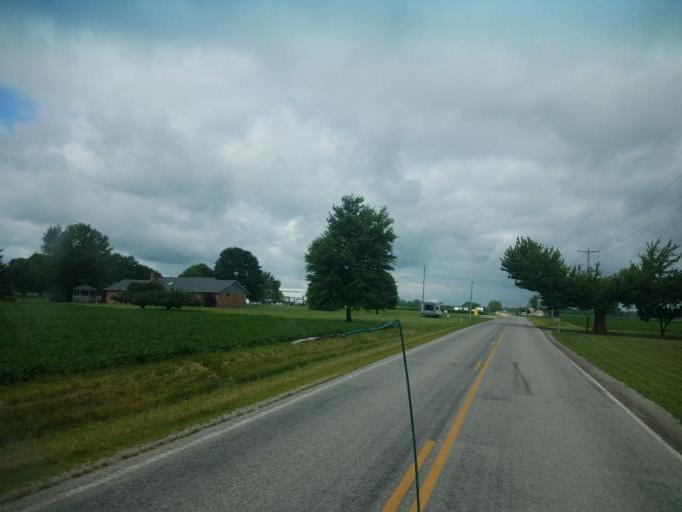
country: US
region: Ohio
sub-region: Union County
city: Richwood
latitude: 40.4030
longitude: -83.4242
